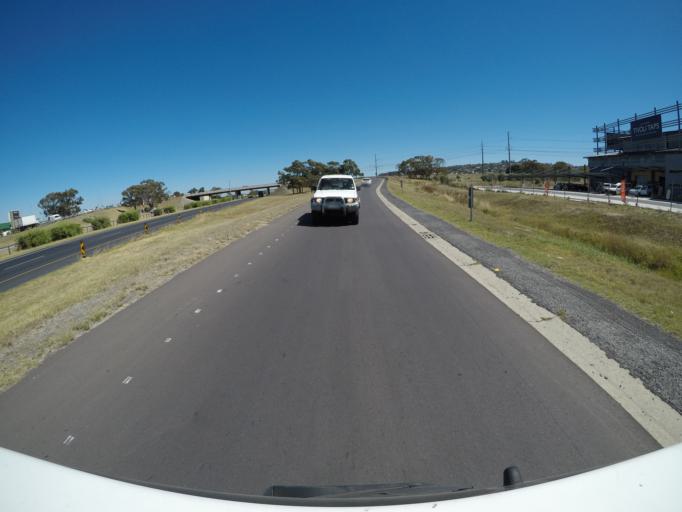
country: ZA
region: Western Cape
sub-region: Cape Winelands District Municipality
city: Stellenbosch
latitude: -34.0782
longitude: 18.8228
